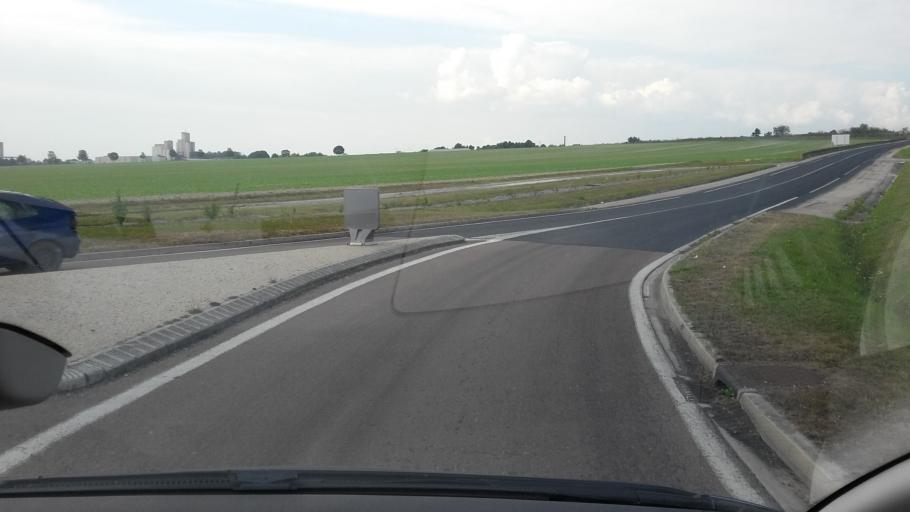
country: FR
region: Champagne-Ardenne
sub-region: Departement de la Marne
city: Fere-Champenoise
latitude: 48.7619
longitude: 4.0009
